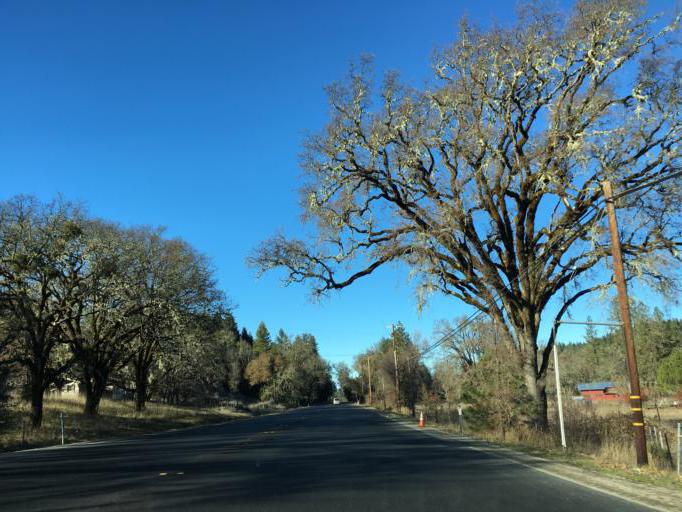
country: US
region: California
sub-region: Mendocino County
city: Laytonville
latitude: 39.6424
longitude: -123.4733
